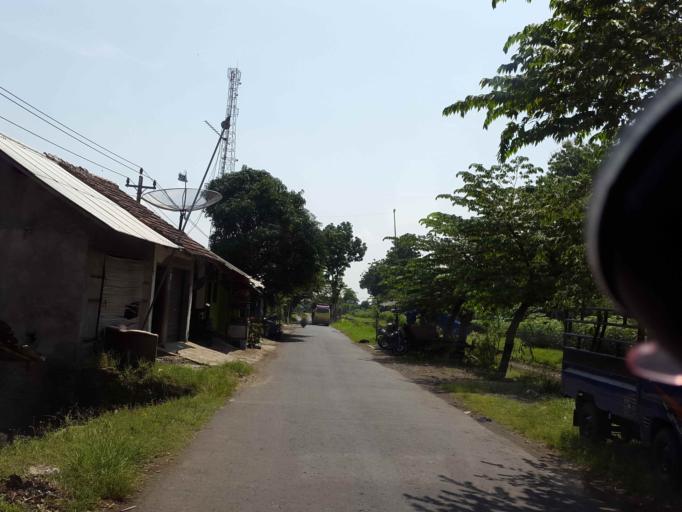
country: ID
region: Central Java
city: Pemalang
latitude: -6.9432
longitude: 109.3869
